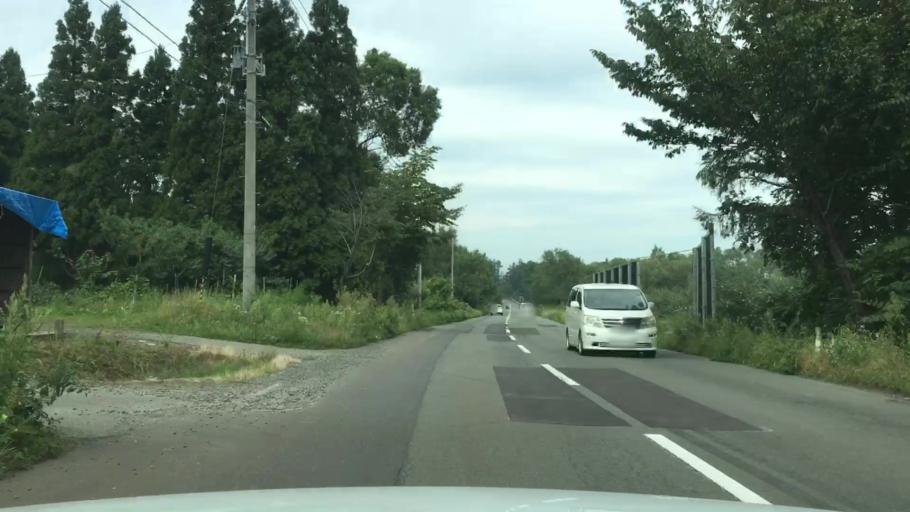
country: JP
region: Aomori
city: Hirosaki
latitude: 40.6811
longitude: 140.3711
